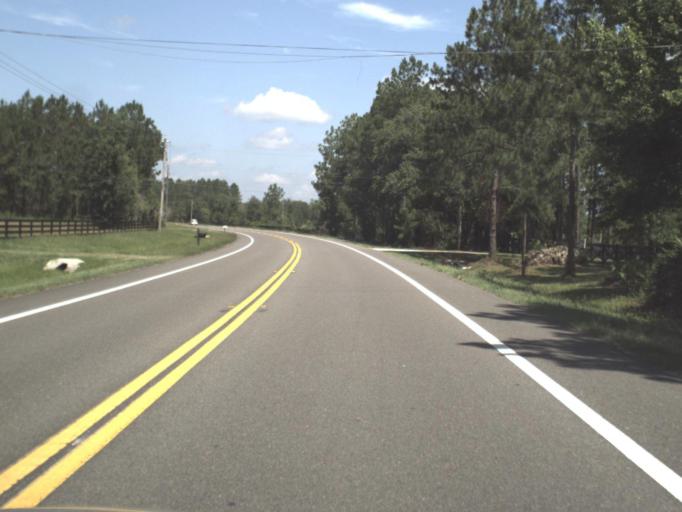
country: US
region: Florida
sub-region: Clay County
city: Green Cove Springs
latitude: 29.9744
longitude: -81.5412
